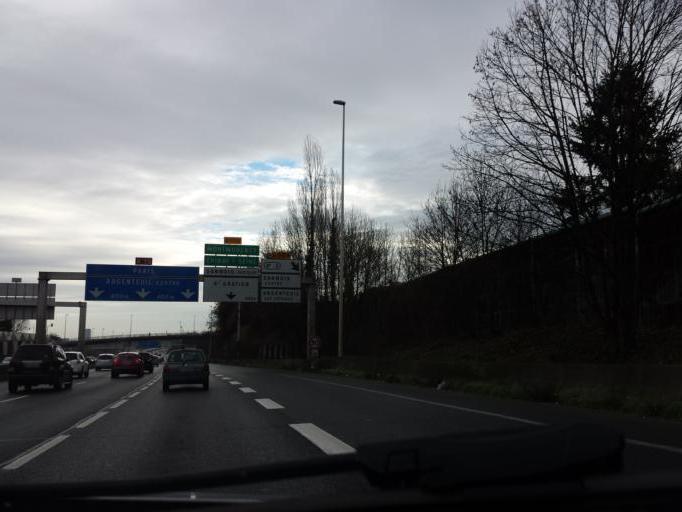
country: FR
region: Ile-de-France
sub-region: Departement du Val-d'Oise
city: Sannois
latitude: 48.9675
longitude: 2.2532
